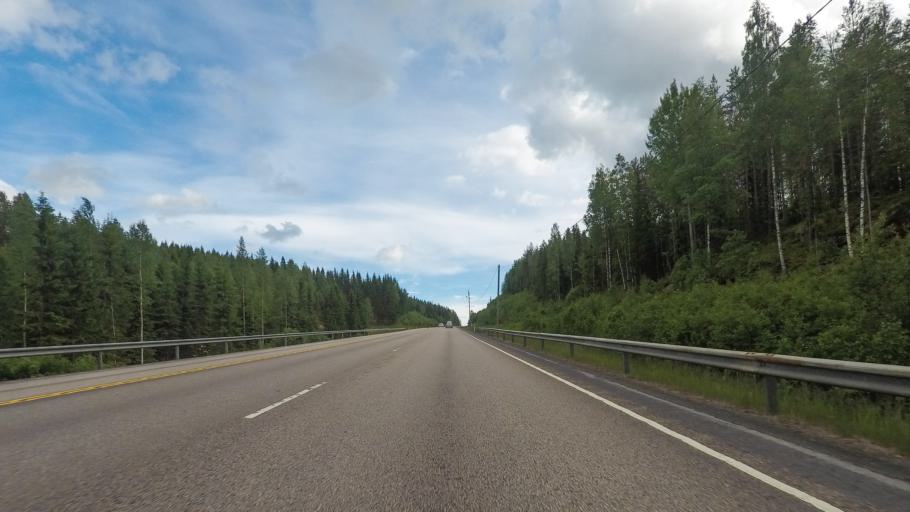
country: FI
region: Central Finland
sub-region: Jyvaeskylae
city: Toivakka
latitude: 62.0526
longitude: 26.0517
